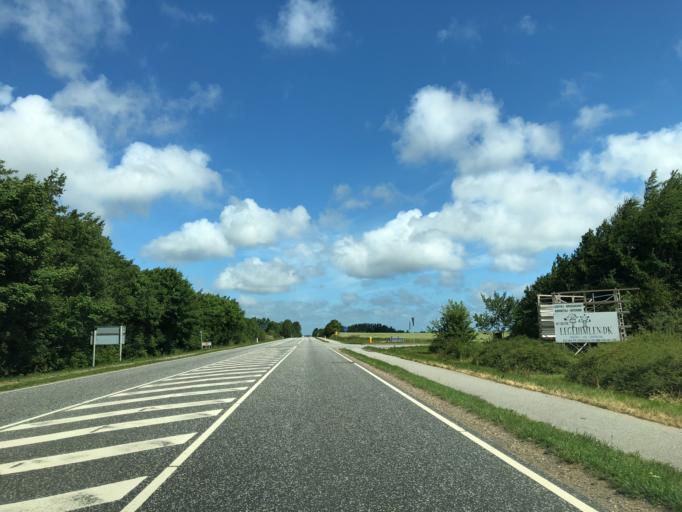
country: DK
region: Central Jutland
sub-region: Struer Kommune
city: Struer
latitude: 56.4348
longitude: 8.5969
